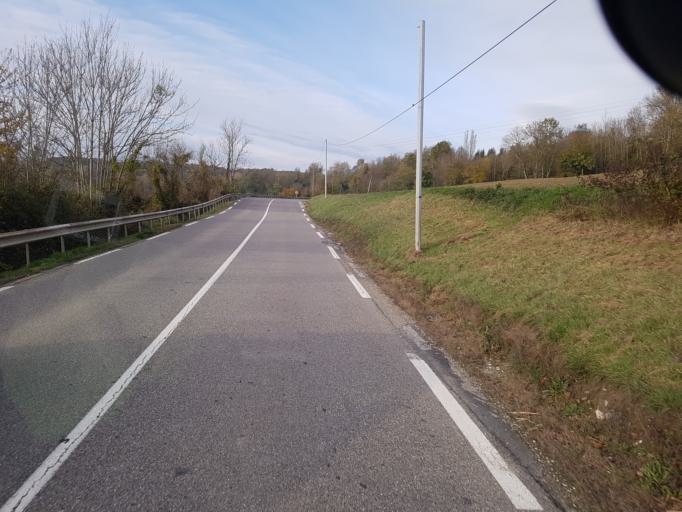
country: FR
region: Rhone-Alpes
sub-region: Departement de la Haute-Savoie
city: Frangy
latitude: 46.0457
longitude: 5.8843
